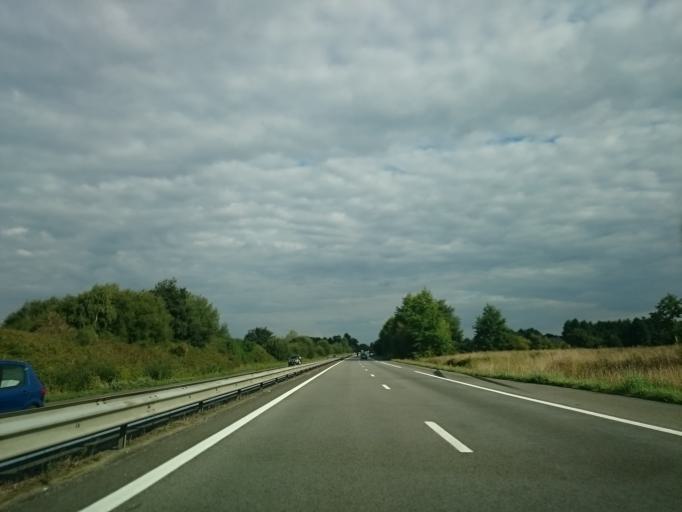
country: FR
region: Pays de la Loire
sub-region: Departement de la Loire-Atlantique
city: Orvault
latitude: 47.2969
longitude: -1.6200
